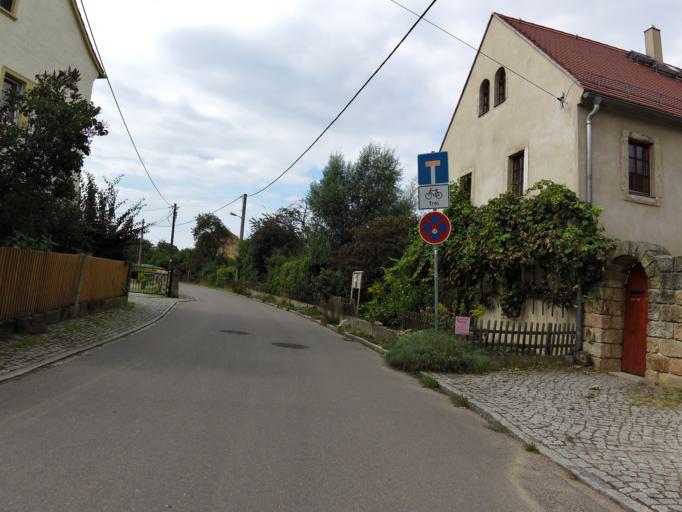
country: DE
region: Saxony
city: Radebeul
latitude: 51.0947
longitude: 13.6421
